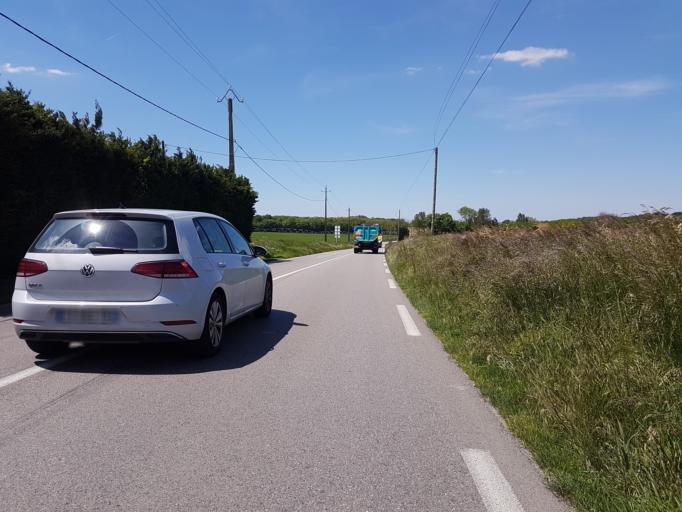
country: FR
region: Rhone-Alpes
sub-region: Departement de l'Isere
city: Chavanoz
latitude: 45.7844
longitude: 5.1517
